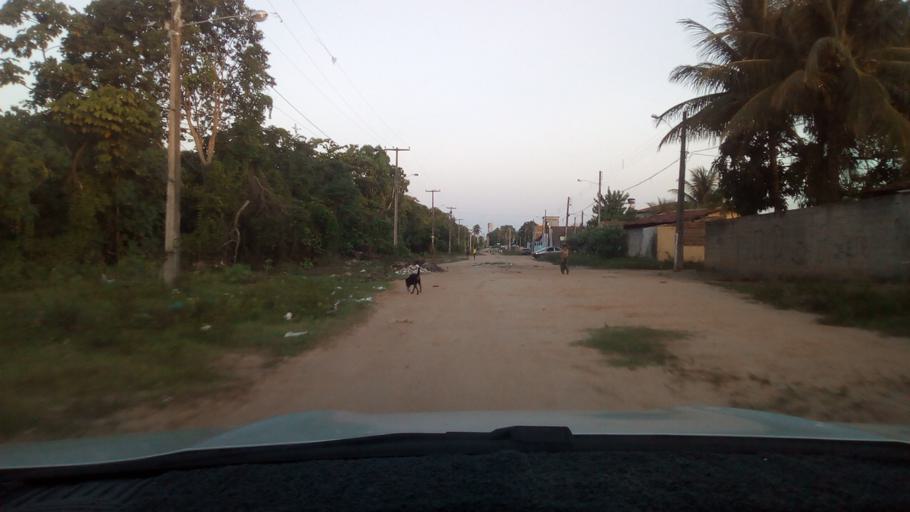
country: BR
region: Paraiba
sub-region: Bayeux
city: Bayeux
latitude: -7.1721
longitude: -34.9279
